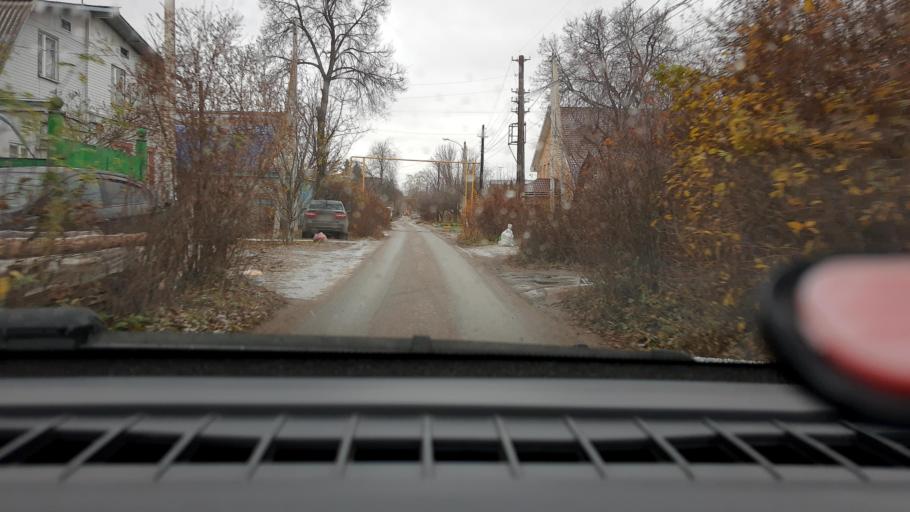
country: RU
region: Nizjnij Novgorod
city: Burevestnik
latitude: 56.2013
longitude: 43.7879
